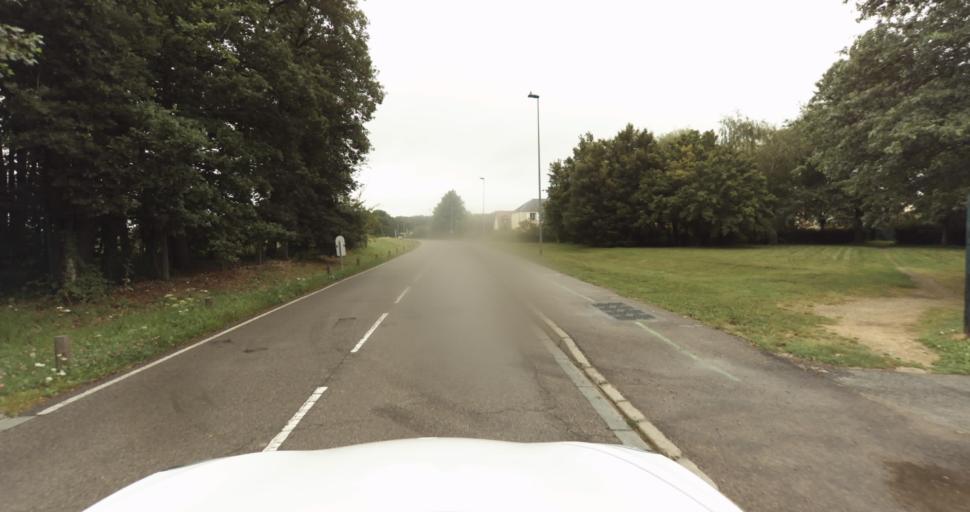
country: FR
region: Haute-Normandie
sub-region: Departement de l'Eure
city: Aviron
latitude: 49.0407
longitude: 1.1292
